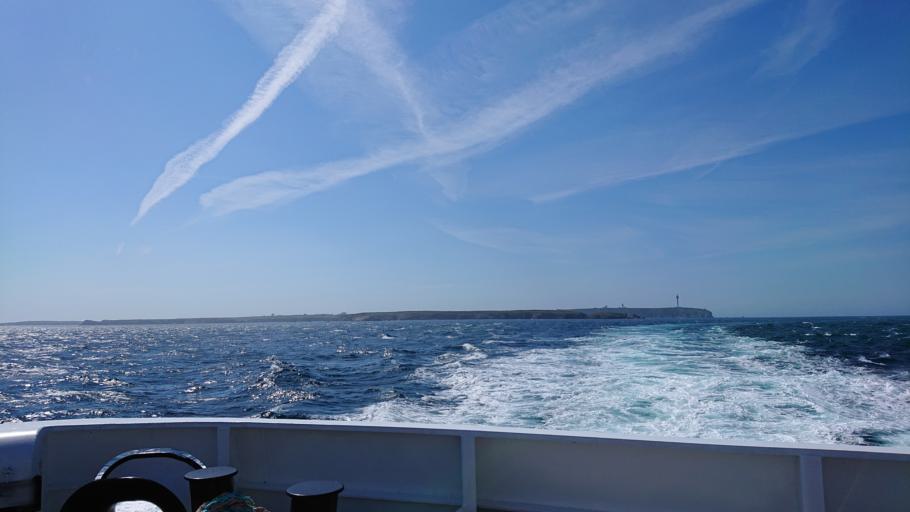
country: FR
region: Brittany
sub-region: Departement du Finistere
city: Porspoder
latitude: 48.4548
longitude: -5.0140
